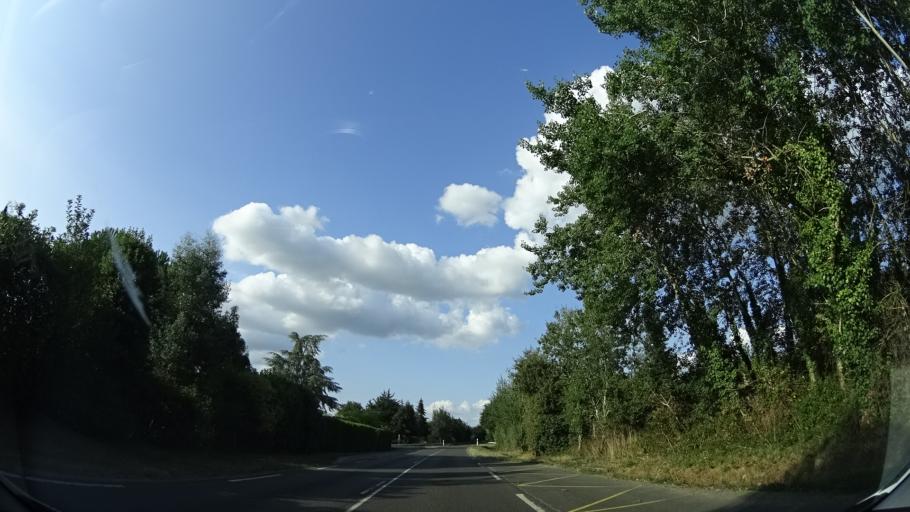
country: FR
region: Pays de la Loire
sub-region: Departement de la Loire-Atlantique
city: Suce-sur-Erdre
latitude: 47.3567
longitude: -1.5299
